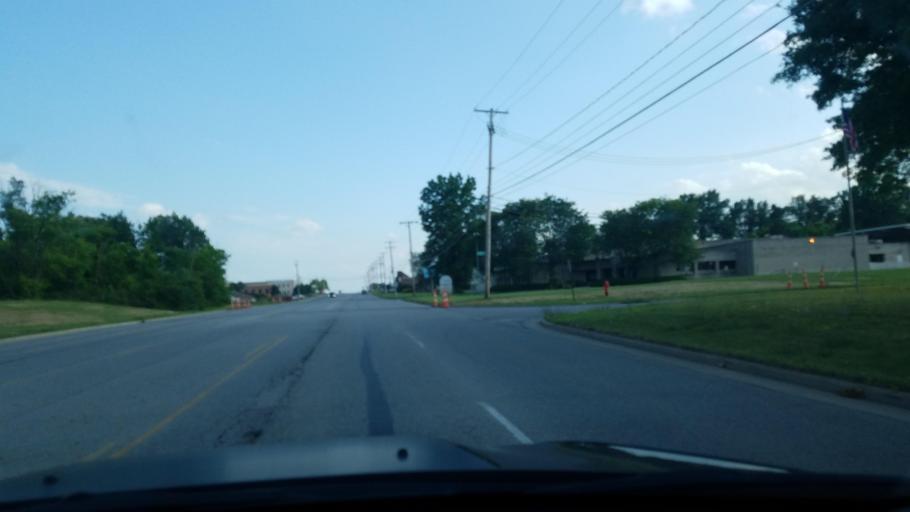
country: US
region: Ohio
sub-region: Mahoning County
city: Poland
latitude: 40.9937
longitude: -80.6338
